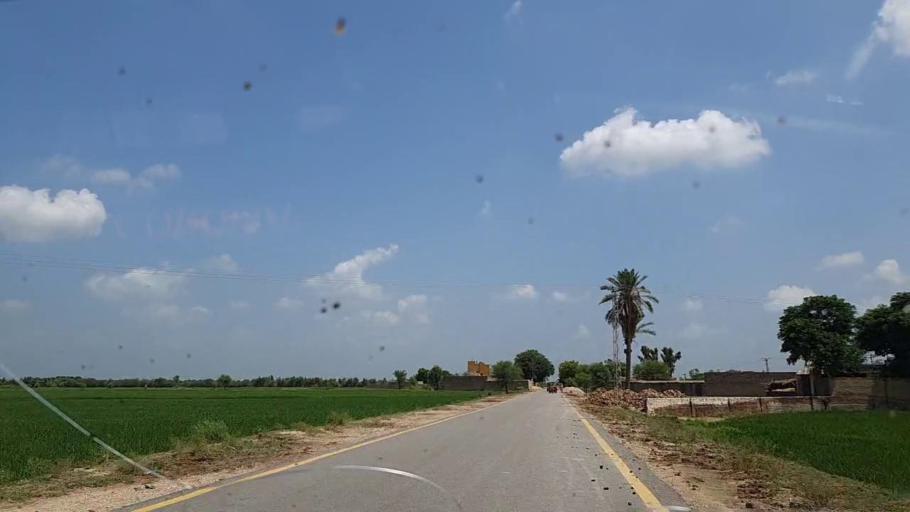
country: PK
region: Sindh
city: Tharu Shah
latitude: 26.9797
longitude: 68.0835
